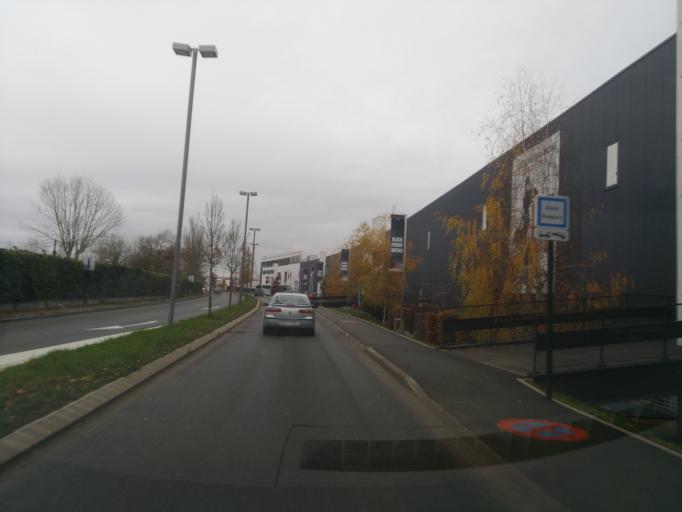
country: FR
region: Ile-de-France
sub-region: Departement des Yvelines
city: Les Clayes-sous-Bois
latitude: 48.8291
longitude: 1.9817
